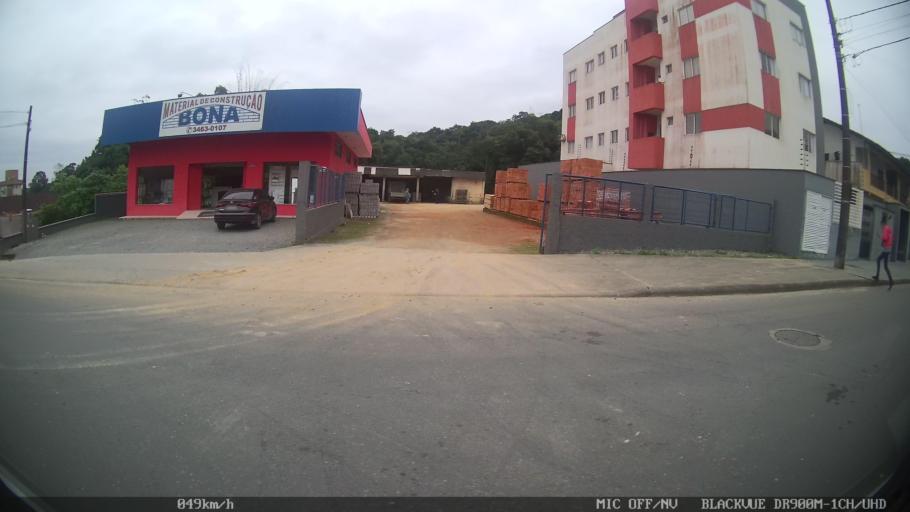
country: BR
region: Santa Catarina
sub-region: Joinville
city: Joinville
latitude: -26.3660
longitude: -48.8461
